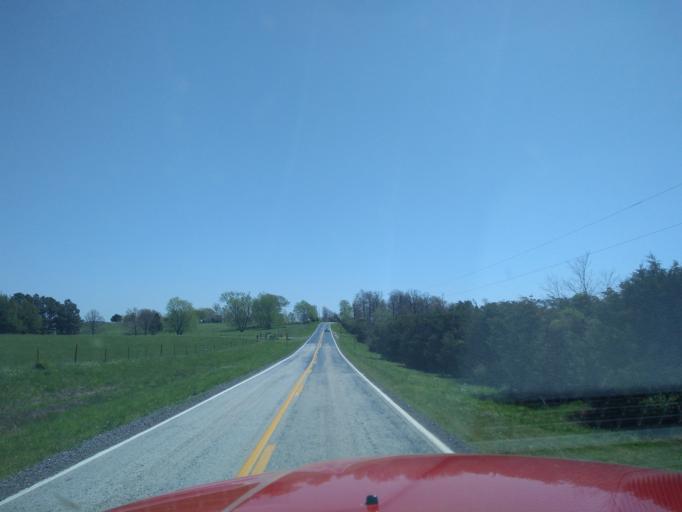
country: US
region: Arkansas
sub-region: Washington County
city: West Fork
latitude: 35.9048
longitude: -94.2253
